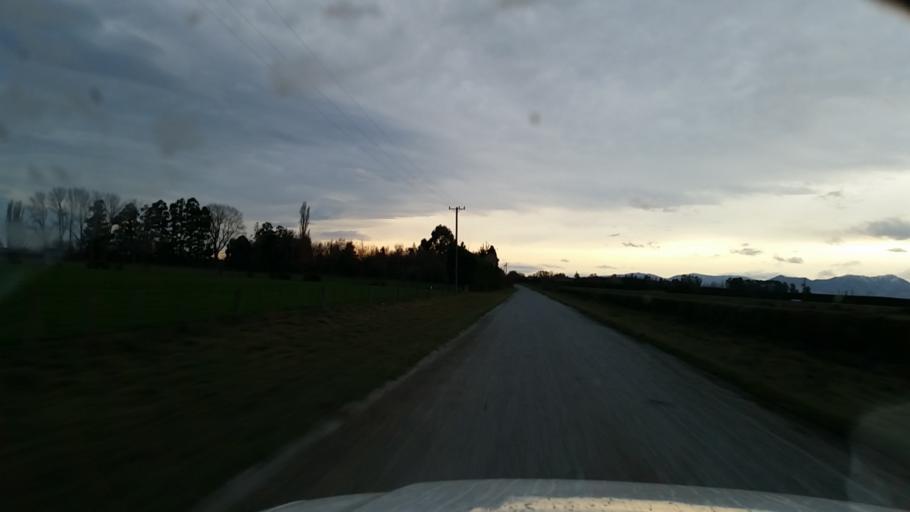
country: NZ
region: Canterbury
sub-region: Ashburton District
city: Ashburton
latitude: -43.8308
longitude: 171.6286
